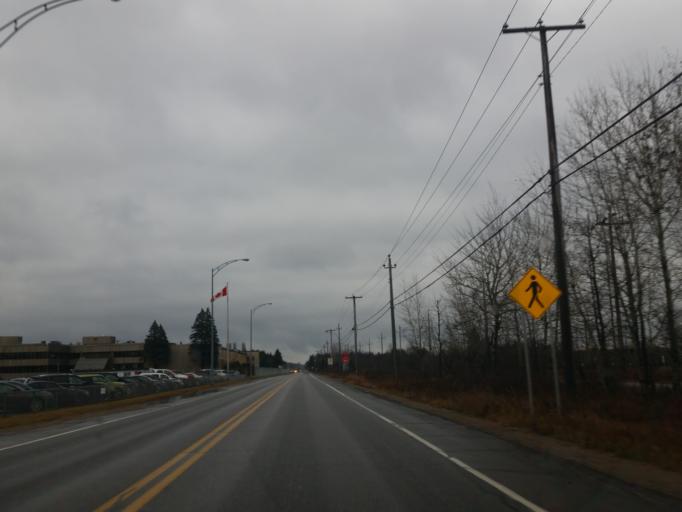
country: CA
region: Quebec
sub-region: Capitale-Nationale
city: Shannon
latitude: 46.8831
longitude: -71.4820
